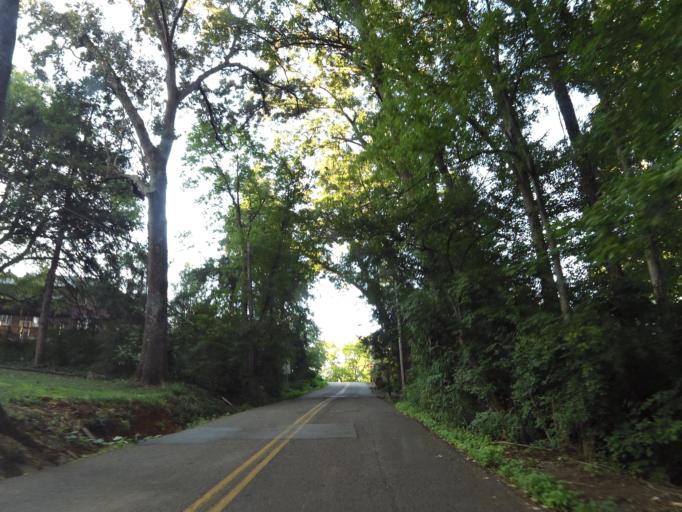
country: US
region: Tennessee
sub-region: Knox County
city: Knoxville
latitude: 35.9445
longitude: -83.9662
